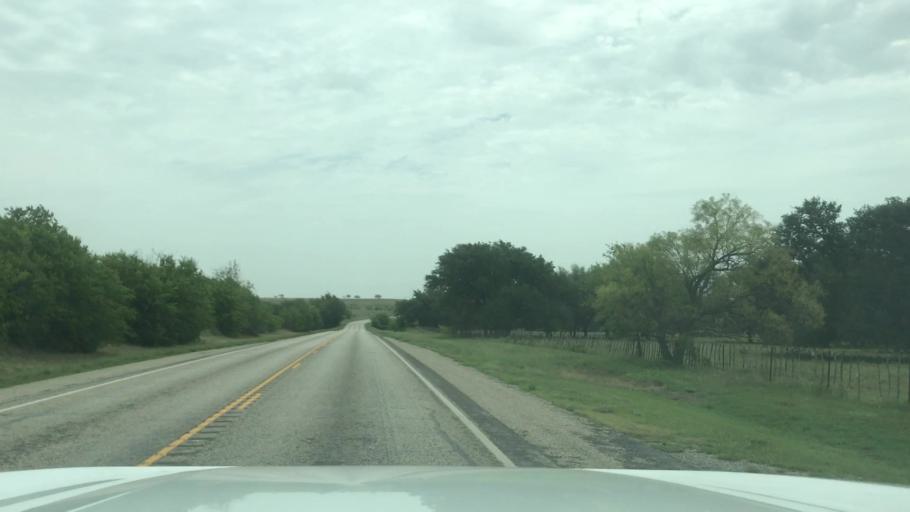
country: US
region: Texas
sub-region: Erath County
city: Dublin
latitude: 32.0576
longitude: -98.1924
